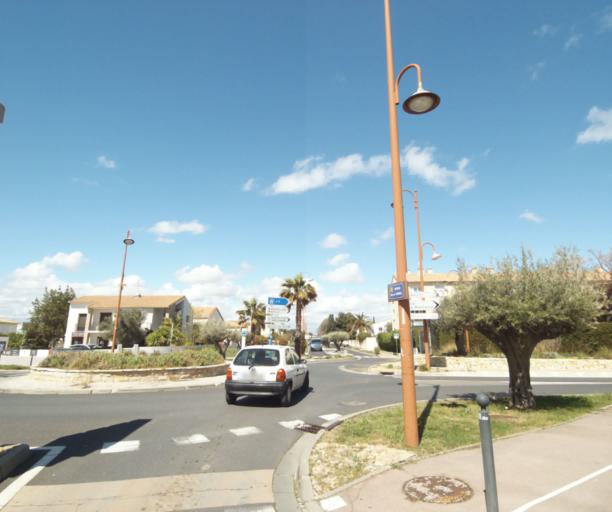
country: FR
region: Languedoc-Roussillon
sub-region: Departement de l'Herault
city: Perols
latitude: 43.5625
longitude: 3.9507
